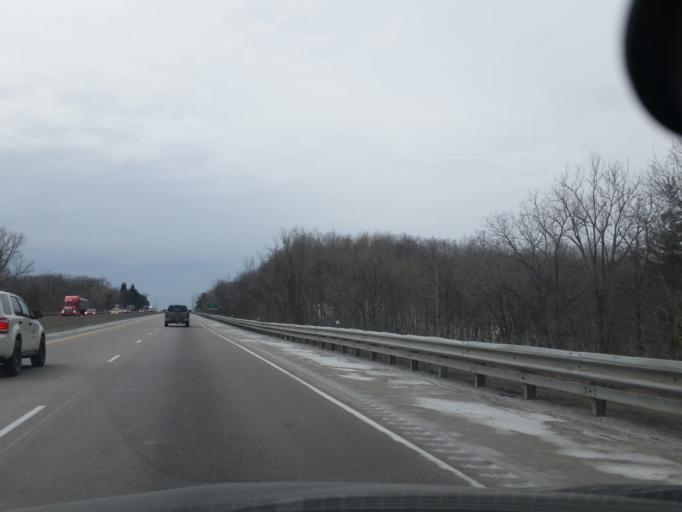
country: CA
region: Ontario
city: Quinte West
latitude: 44.1168
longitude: -77.6446
